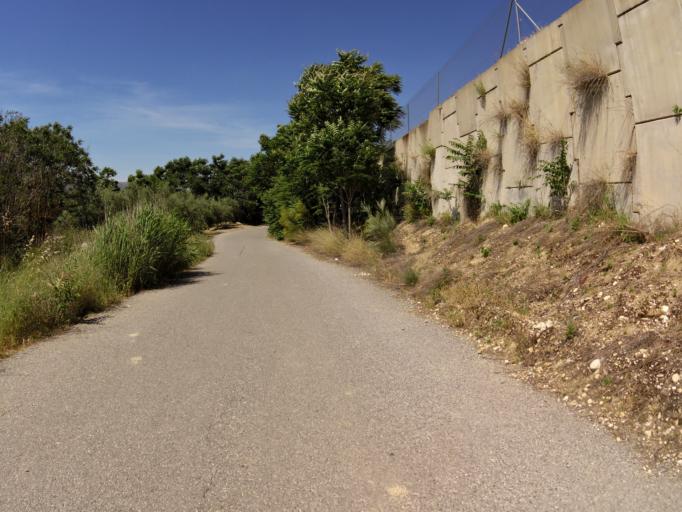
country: ES
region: Andalusia
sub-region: Provincia de Granada
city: Salar
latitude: 37.1782
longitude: -4.0811
